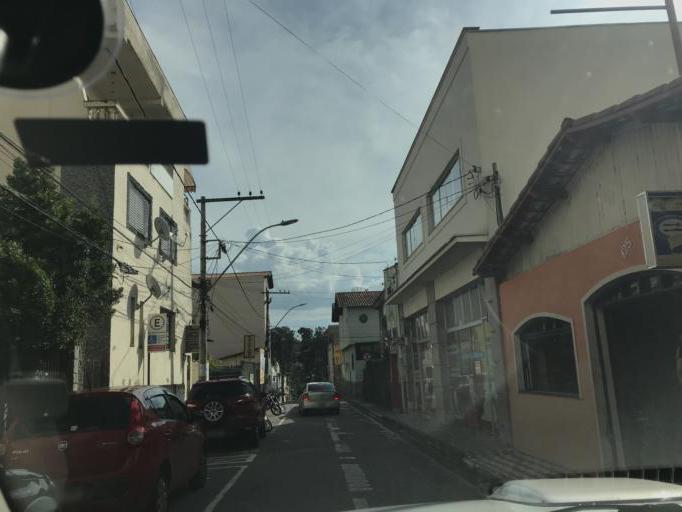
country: BR
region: Minas Gerais
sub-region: Tres Coracoes
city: Tres Coracoes
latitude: -21.7001
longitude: -45.2567
